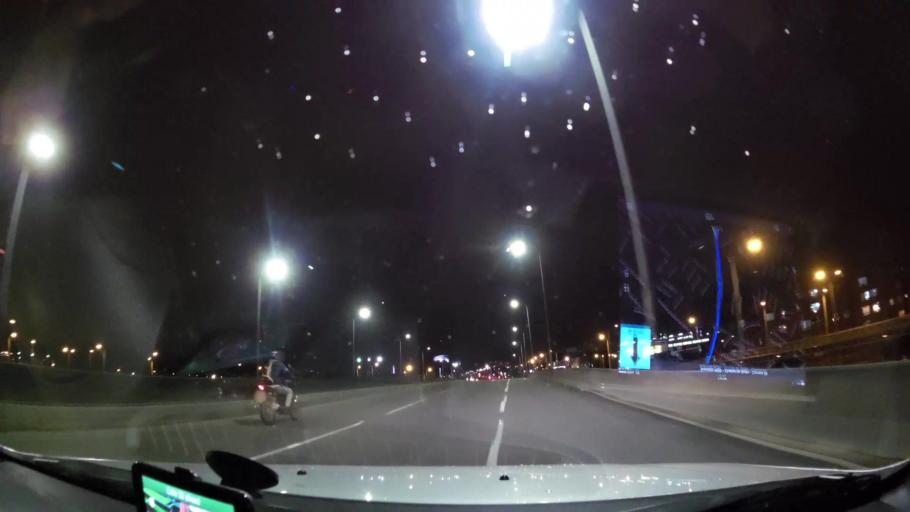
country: CO
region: Bogota D.C.
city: Bogota
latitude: 4.5936
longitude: -74.1269
